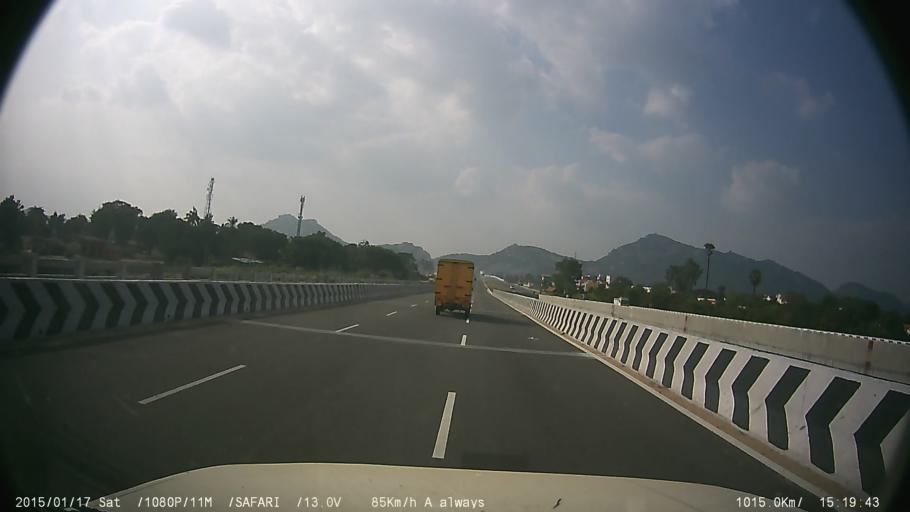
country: IN
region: Tamil Nadu
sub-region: Krishnagiri
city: Krishnagiri
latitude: 12.5980
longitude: 78.1351
